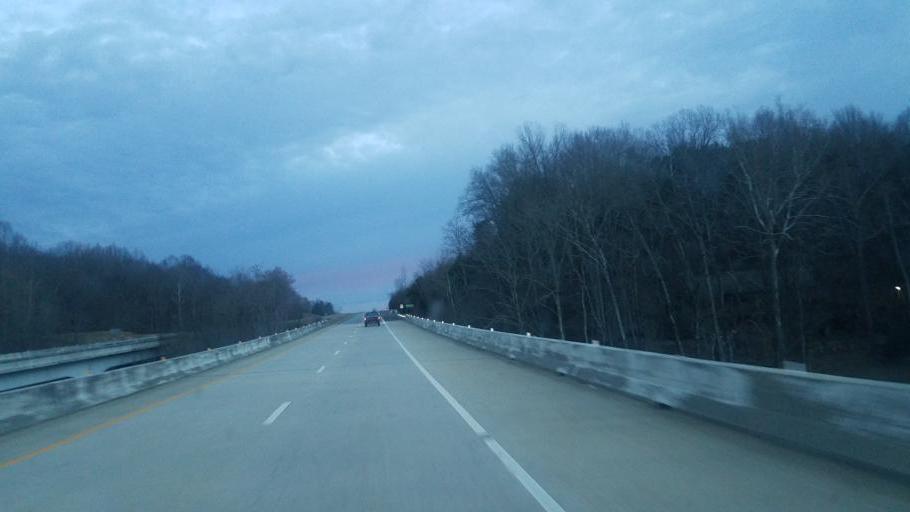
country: US
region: Tennessee
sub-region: Van Buren County
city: Spencer
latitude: 35.8214
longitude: -85.4611
